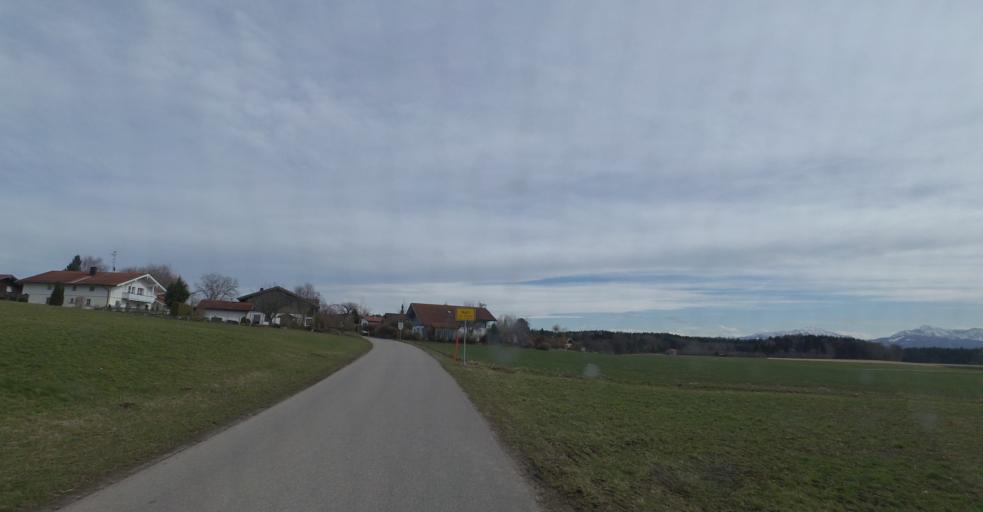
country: DE
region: Bavaria
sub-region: Upper Bavaria
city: Chieming
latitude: 47.9286
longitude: 12.5443
